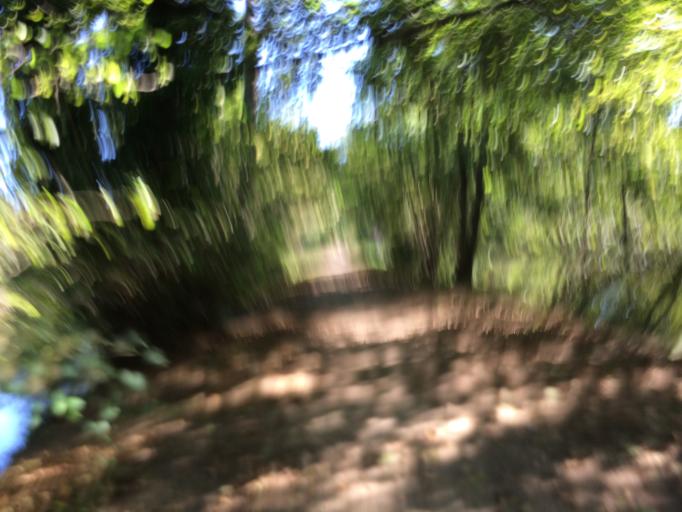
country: FR
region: Ile-de-France
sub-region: Departement de l'Essonne
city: Orsay
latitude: 48.7025
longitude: 2.2033
